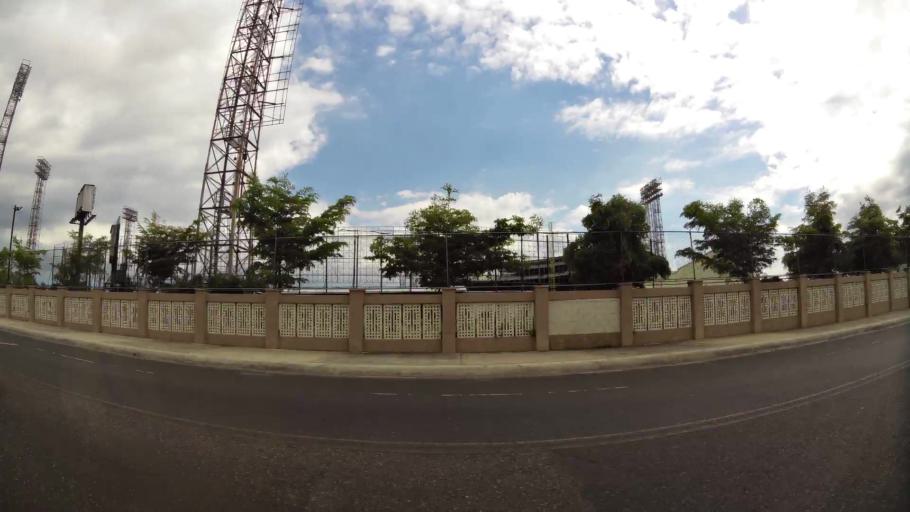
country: DO
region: Nacional
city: La Agustina
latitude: 18.4896
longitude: -69.9265
